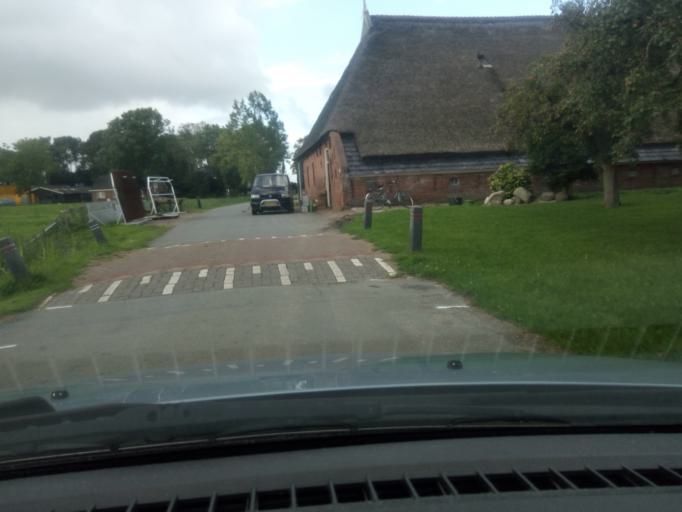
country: NL
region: Groningen
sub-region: Gemeente Grootegast
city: Grootegast
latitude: 53.2643
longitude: 6.2503
